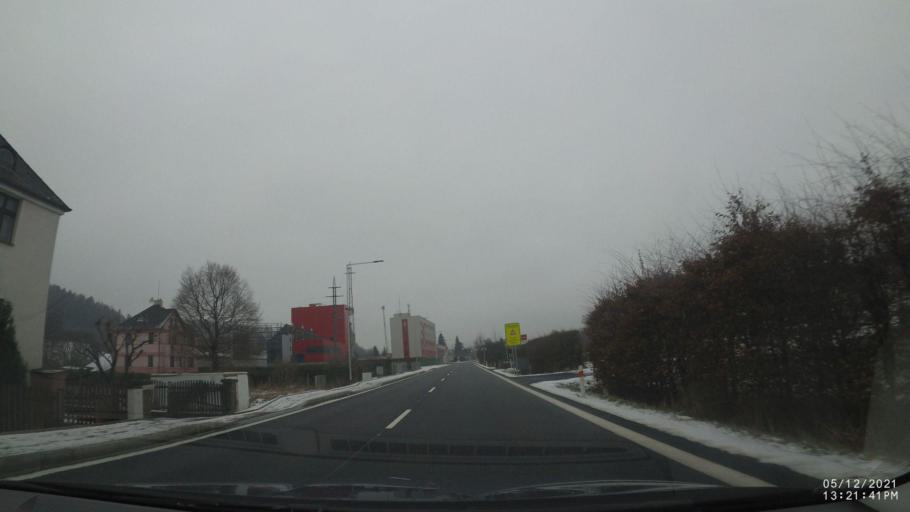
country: CZ
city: Velke Porici
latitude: 50.4597
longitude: 16.1854
